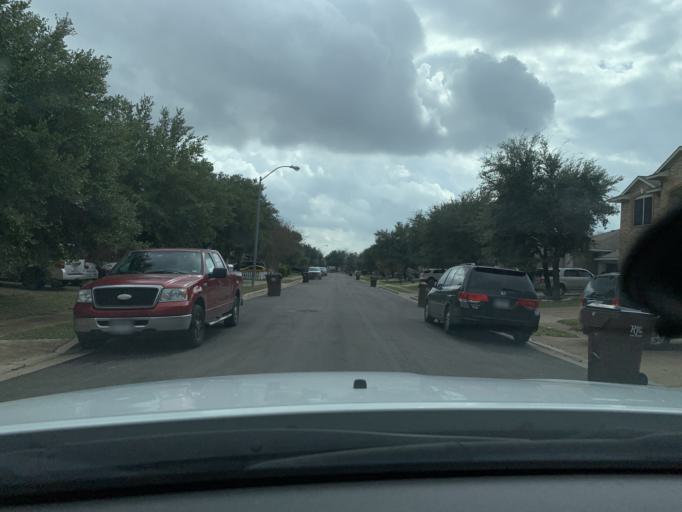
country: US
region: Texas
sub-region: Williamson County
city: Round Rock
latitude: 30.5640
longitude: -97.6651
